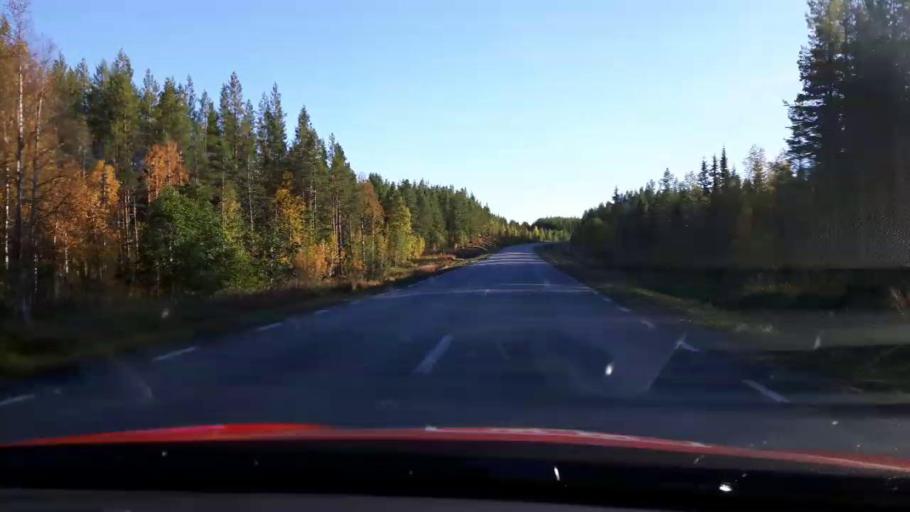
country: SE
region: Jaemtland
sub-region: OEstersunds Kommun
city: Lit
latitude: 63.7641
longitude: 14.7219
